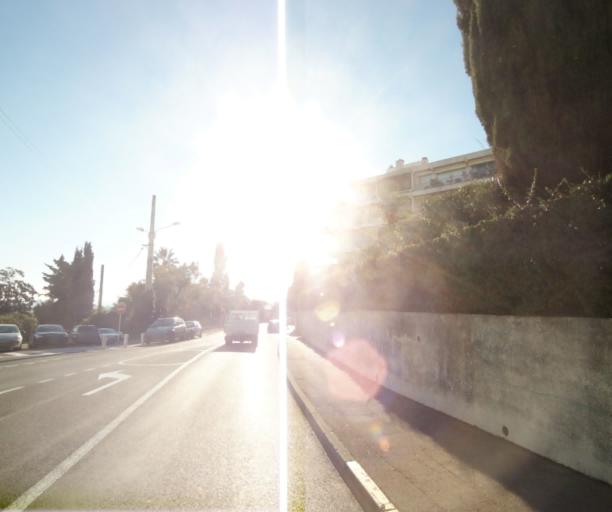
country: FR
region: Provence-Alpes-Cote d'Azur
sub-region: Departement des Alpes-Maritimes
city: Antibes
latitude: 43.5832
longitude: 7.1089
